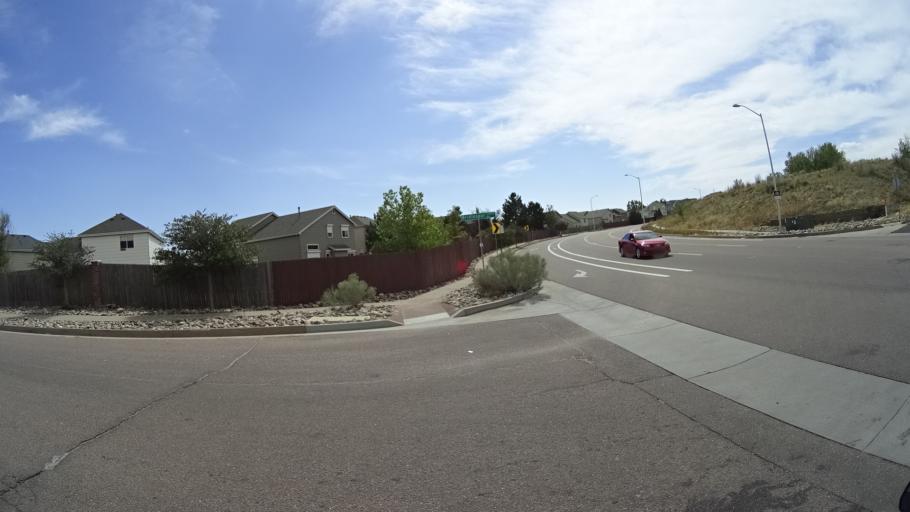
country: US
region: Colorado
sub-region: El Paso County
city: Cimarron Hills
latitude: 38.9074
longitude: -104.7156
